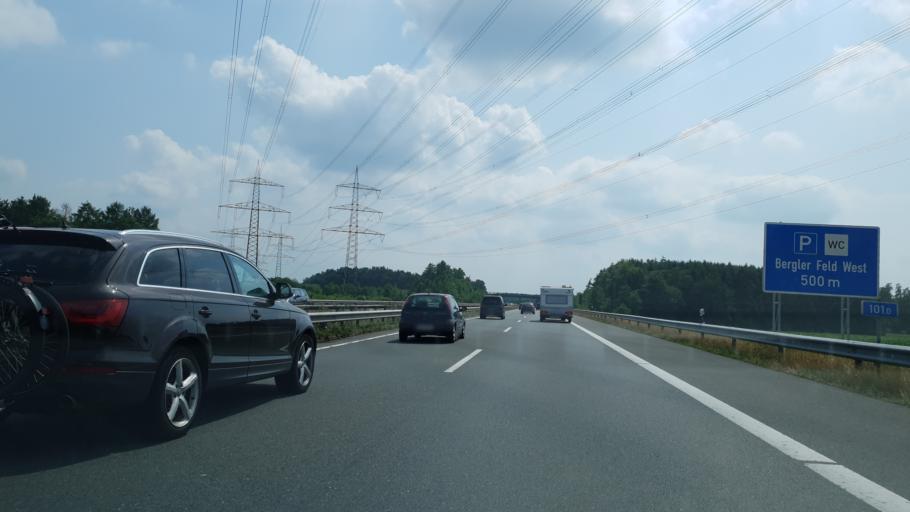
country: DE
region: Lower Saxony
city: Emsburen
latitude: 52.4016
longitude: 7.2505
